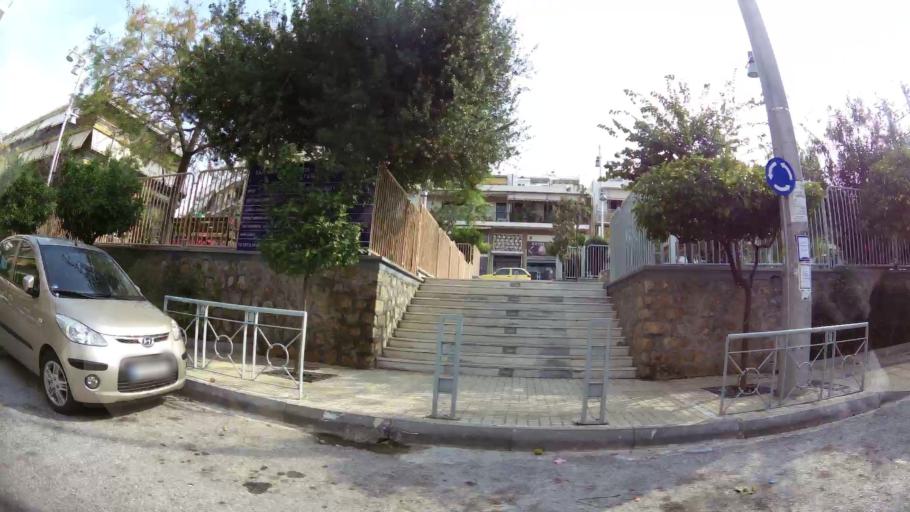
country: GR
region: Attica
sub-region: Nomarchia Athinas
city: Galatsi
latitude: 38.0157
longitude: 23.7582
